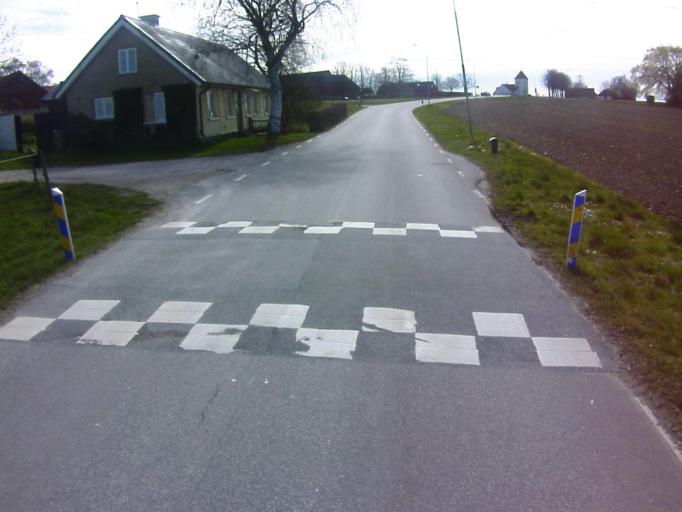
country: SE
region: Skane
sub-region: Kavlinge Kommun
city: Hofterup
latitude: 55.7871
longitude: 12.9739
